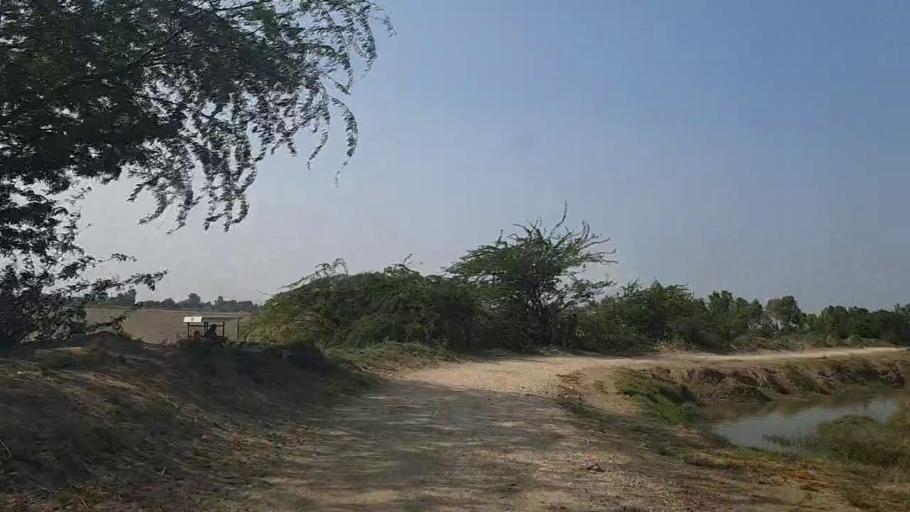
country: PK
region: Sindh
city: Mirpur Sakro
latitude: 24.5646
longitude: 67.8278
